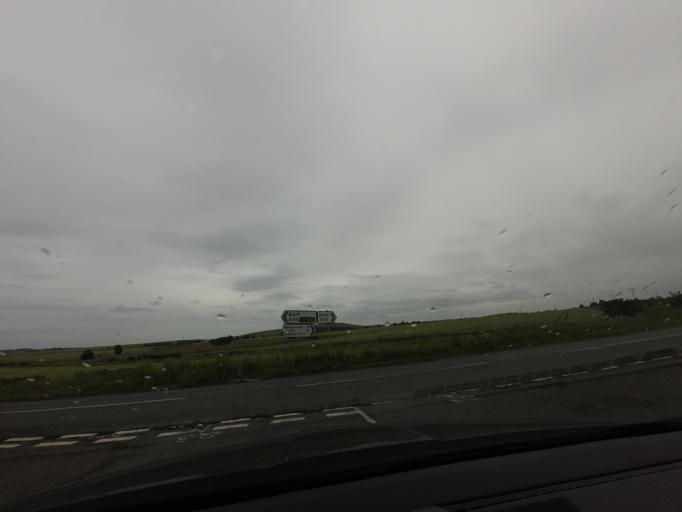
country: GB
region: Scotland
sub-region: Aberdeenshire
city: Portsoy
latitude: 57.6417
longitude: -2.6503
